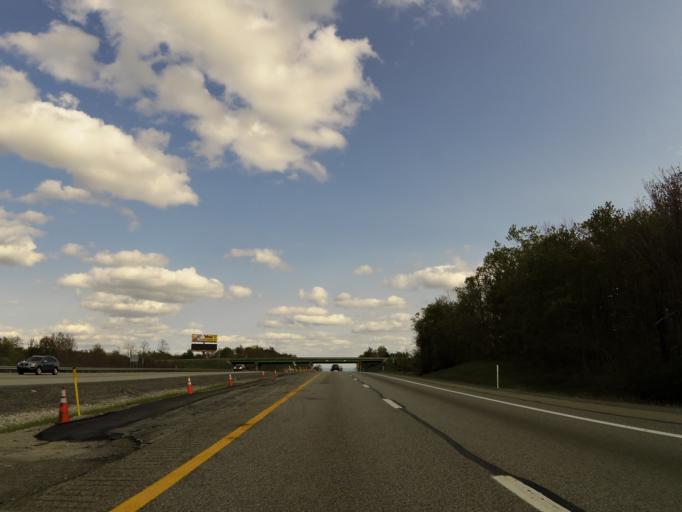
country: US
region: West Virginia
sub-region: Raleigh County
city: Shady Spring
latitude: 37.5829
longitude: -81.1203
